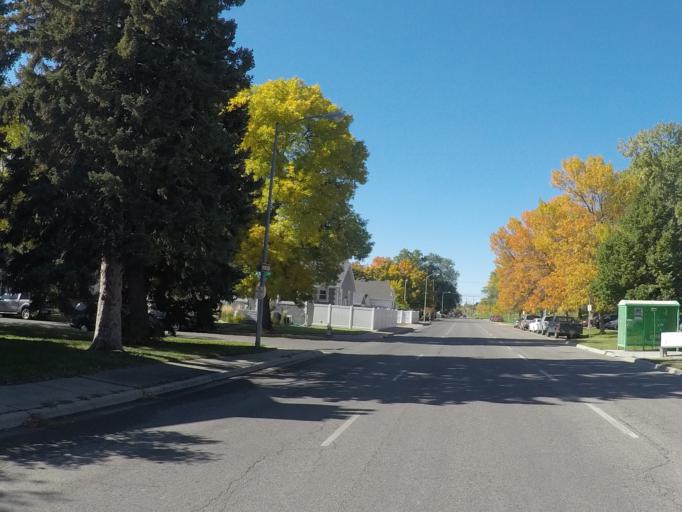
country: US
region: Montana
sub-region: Yellowstone County
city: Billings
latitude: 45.7949
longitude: -108.5231
